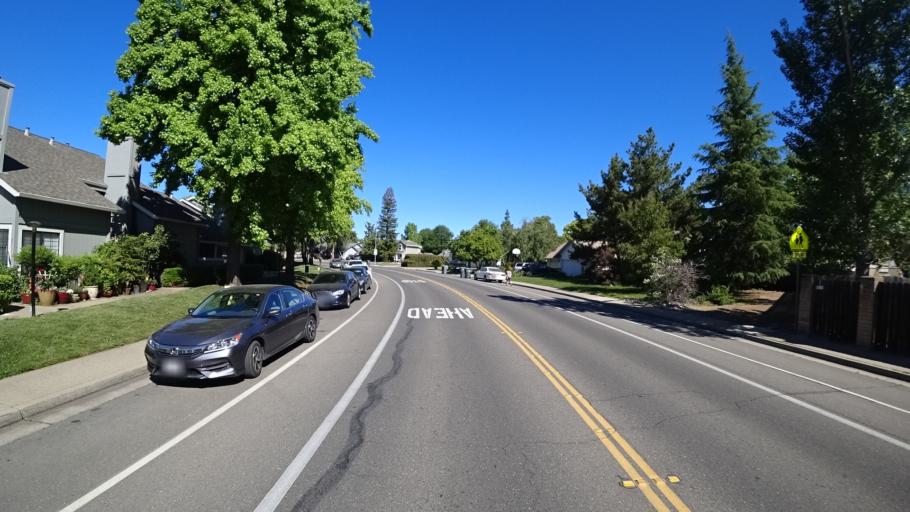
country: US
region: California
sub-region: Placer County
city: Rocklin
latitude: 38.7770
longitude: -121.2551
